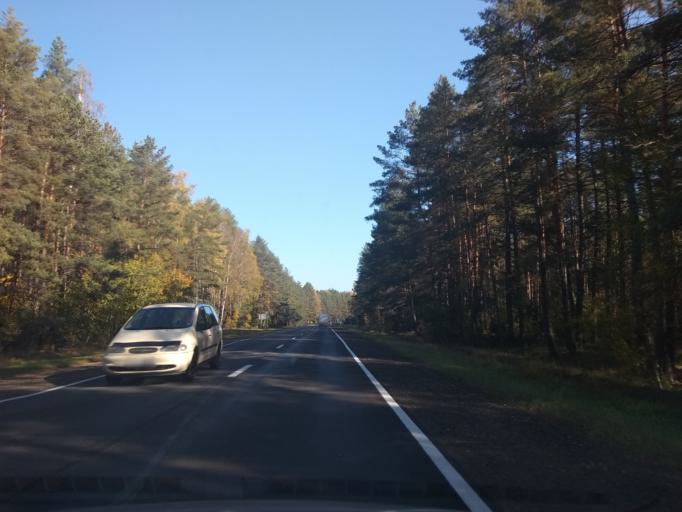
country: BY
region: Brest
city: Baranovichi
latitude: 53.0452
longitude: 25.8218
